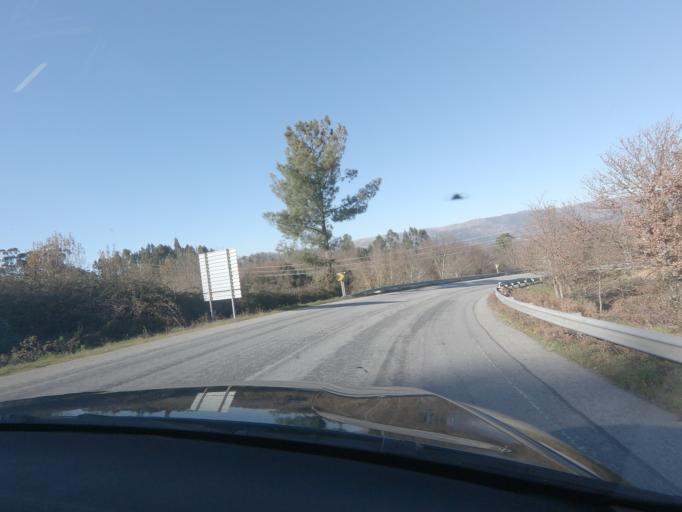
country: PT
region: Viseu
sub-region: Vouzela
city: Vouzela
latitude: 40.7224
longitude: -8.1332
